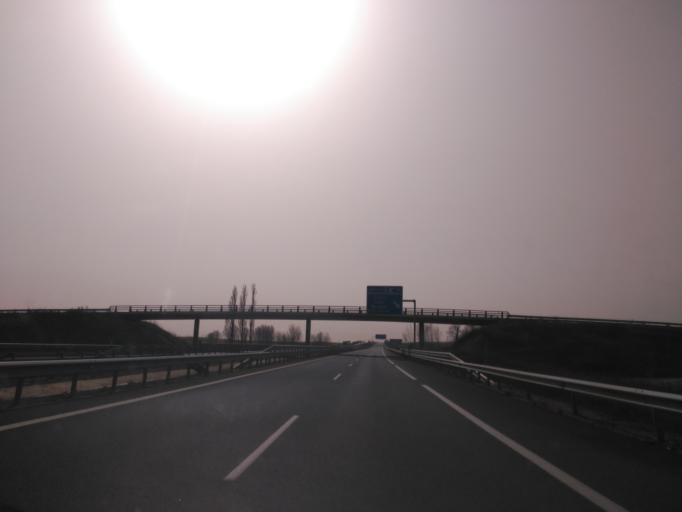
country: ES
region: Castille and Leon
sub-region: Provincia de Palencia
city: Abia de las Torres
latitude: 42.4225
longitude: -4.3888
